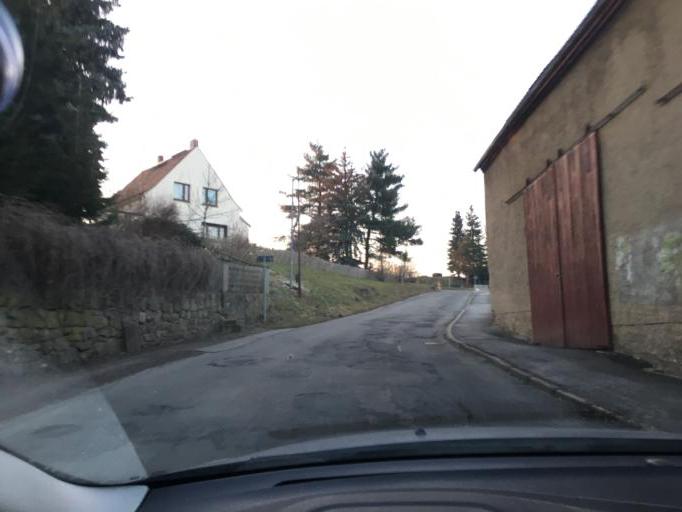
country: DE
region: Saxony
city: Lunzenau
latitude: 50.9632
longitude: 12.7525
